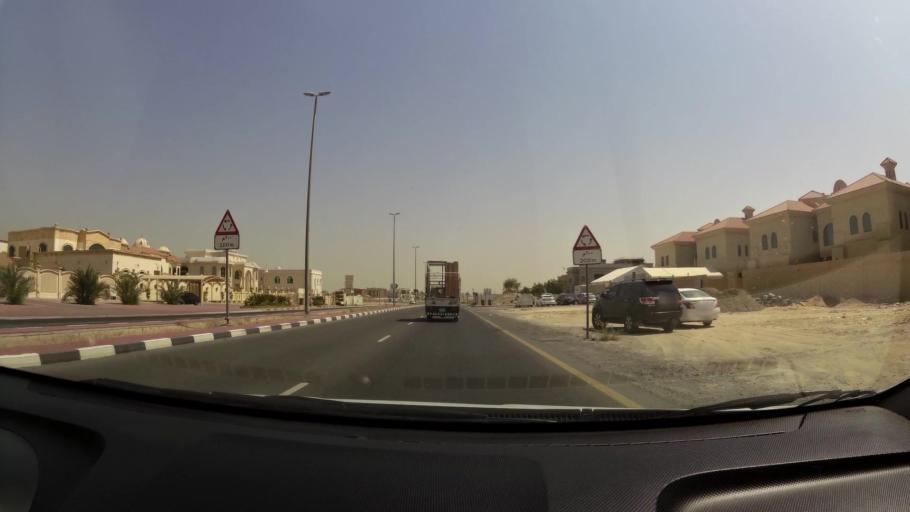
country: AE
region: Ajman
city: Ajman
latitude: 25.4117
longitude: 55.5267
